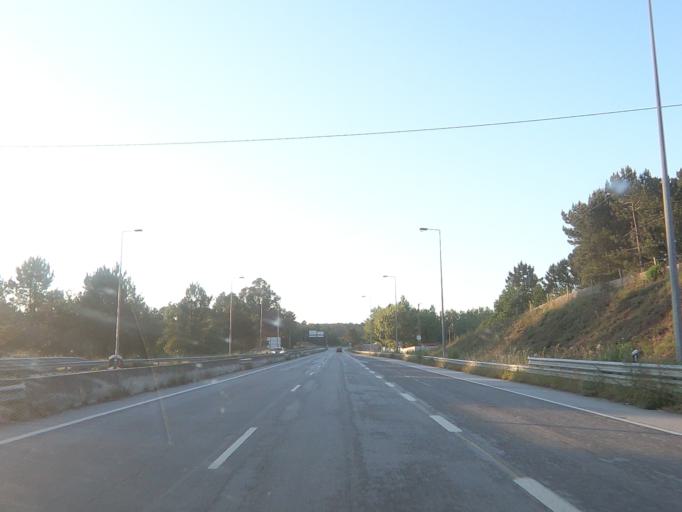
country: PT
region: Viseu
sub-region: Viseu
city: Rio de Loba
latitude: 40.6557
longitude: -7.8621
